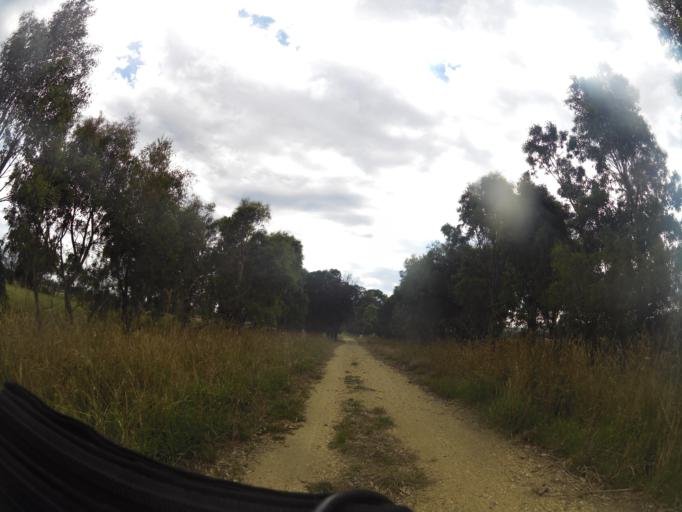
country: AU
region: Victoria
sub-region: Wellington
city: Heyfield
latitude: -38.0496
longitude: 146.6323
